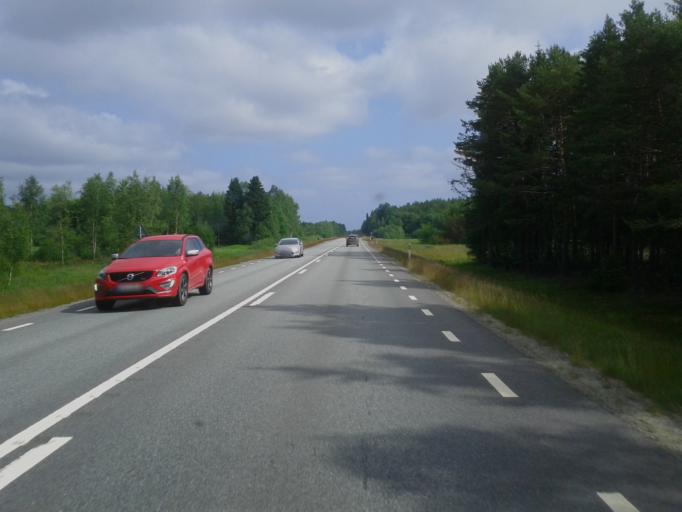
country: SE
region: Vaesterbotten
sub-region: Skelleftea Kommun
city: Burea
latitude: 64.3362
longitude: 21.2709
